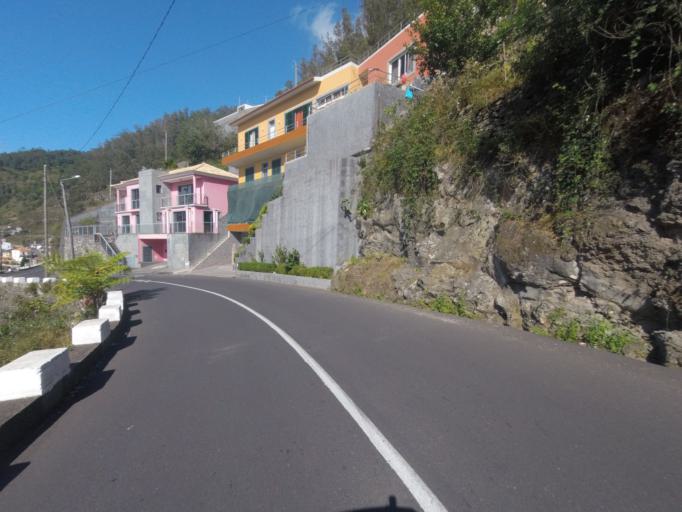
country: PT
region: Madeira
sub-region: Ribeira Brava
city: Campanario
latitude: 32.6670
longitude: -17.0226
